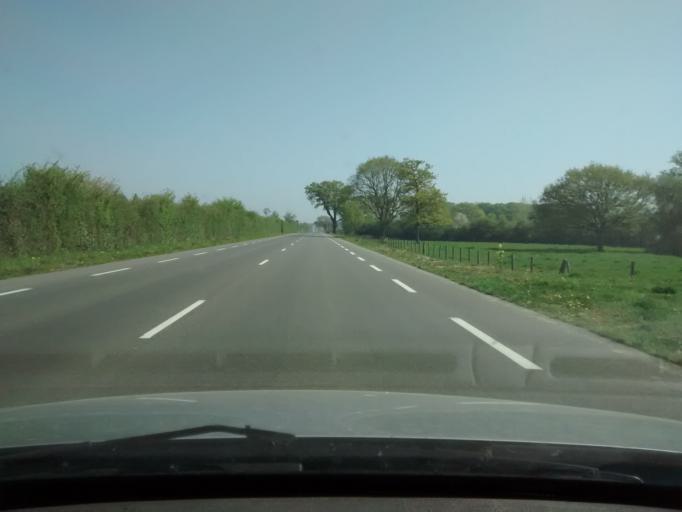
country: FR
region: Pays de la Loire
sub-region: Departement de la Mayenne
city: Soulge-sur-Ouette
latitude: 48.0778
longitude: -0.5474
